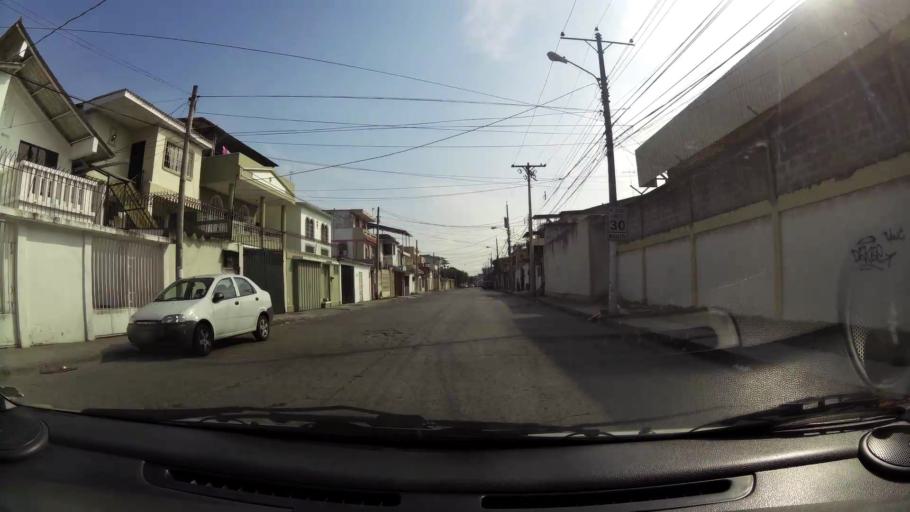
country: EC
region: Guayas
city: Guayaquil
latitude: -2.1880
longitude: -79.9104
